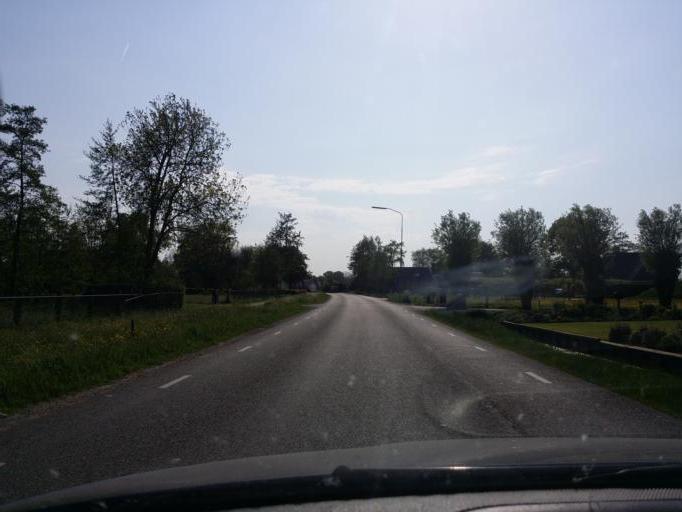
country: NL
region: Groningen
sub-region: Gemeente Grootegast
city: Grootegast
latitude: 53.2182
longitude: 6.2927
